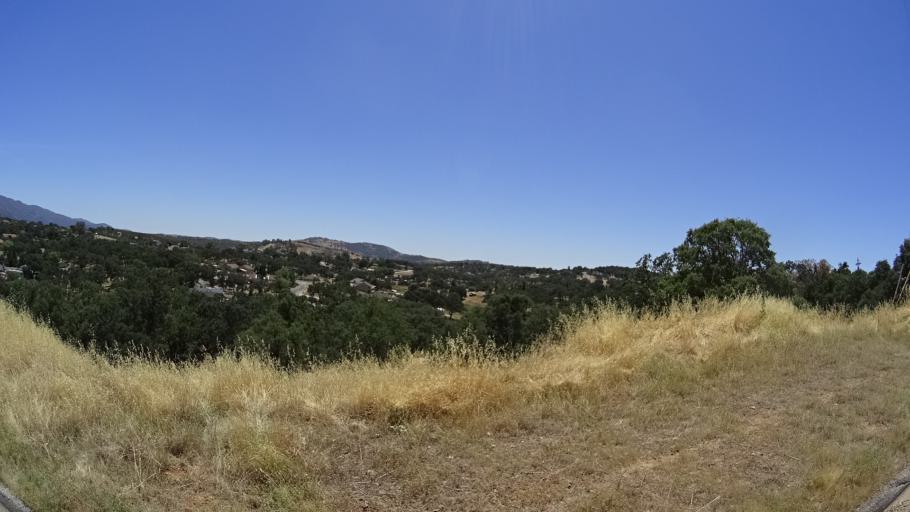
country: US
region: California
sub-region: Calaveras County
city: Valley Springs
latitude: 38.1620
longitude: -120.8373
